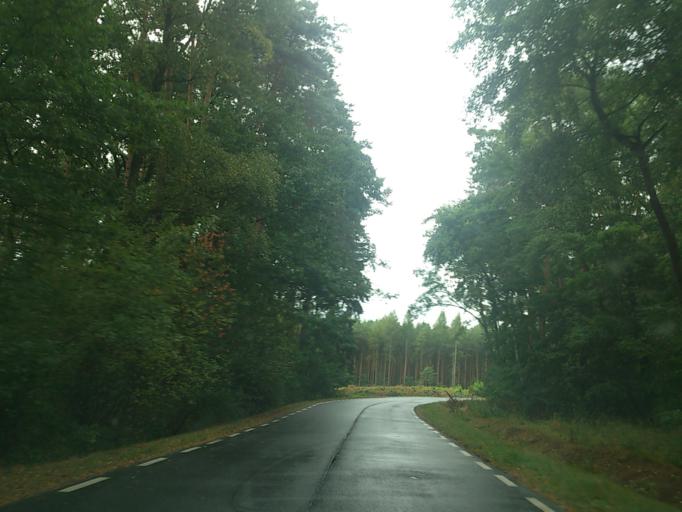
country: PL
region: Greater Poland Voivodeship
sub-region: Powiat poznanski
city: Pobiedziska
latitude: 52.5105
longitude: 17.2018
